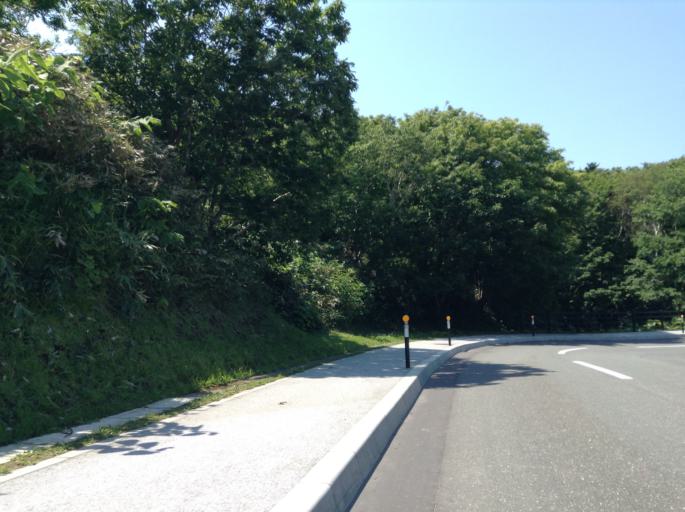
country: JP
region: Hokkaido
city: Wakkanai
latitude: 45.4195
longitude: 141.6693
